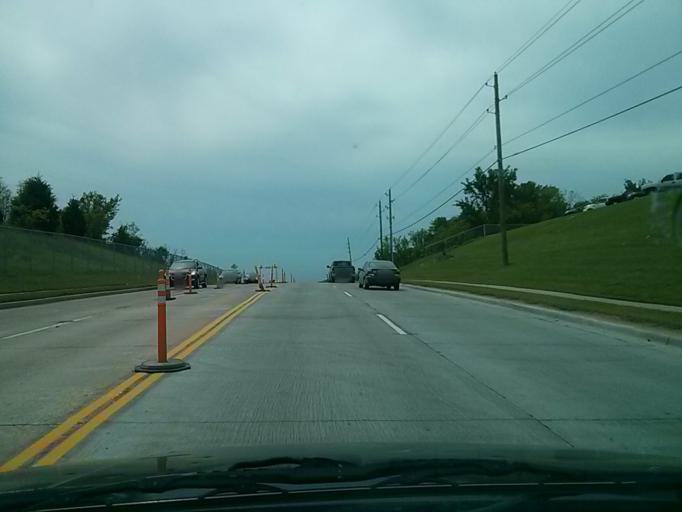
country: US
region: Oklahoma
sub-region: Tulsa County
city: Jenks
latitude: 36.0727
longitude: -95.9042
